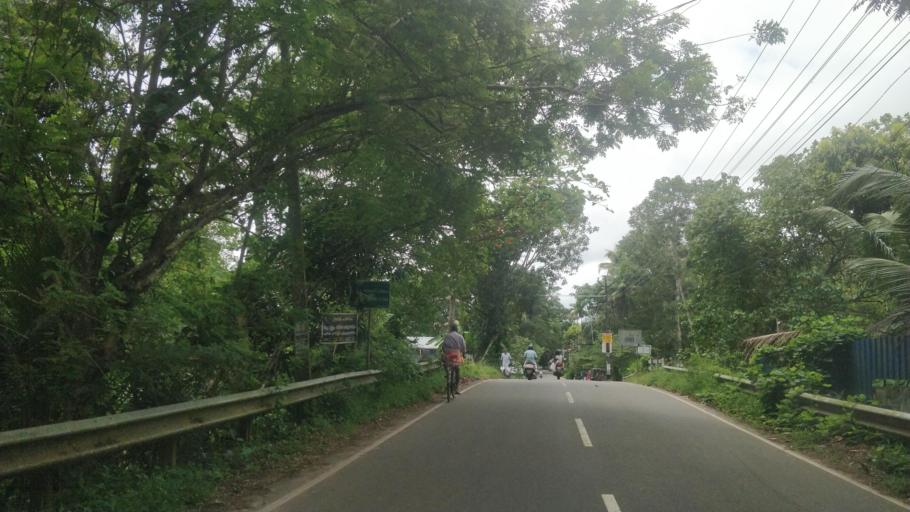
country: IN
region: Kerala
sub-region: Alappuzha
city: Shertallai
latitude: 9.6571
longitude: 76.3673
